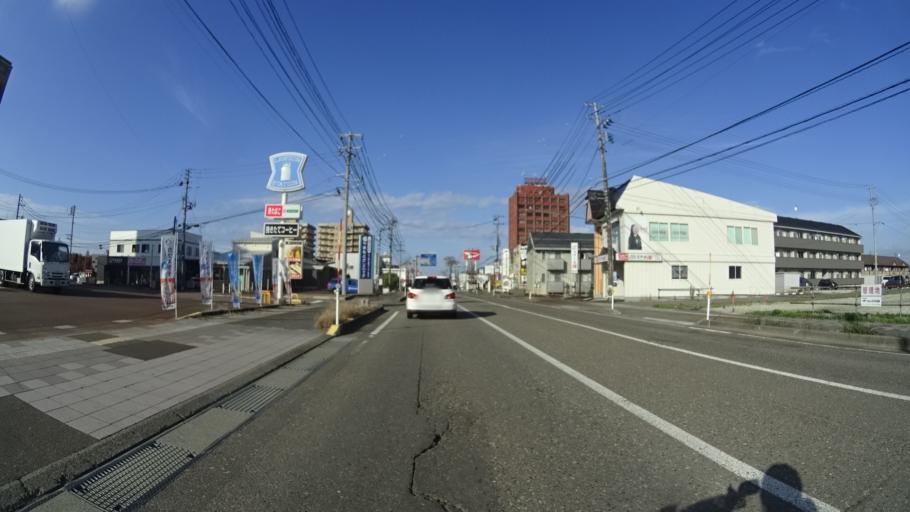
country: JP
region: Niigata
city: Joetsu
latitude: 37.1467
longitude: 138.2397
